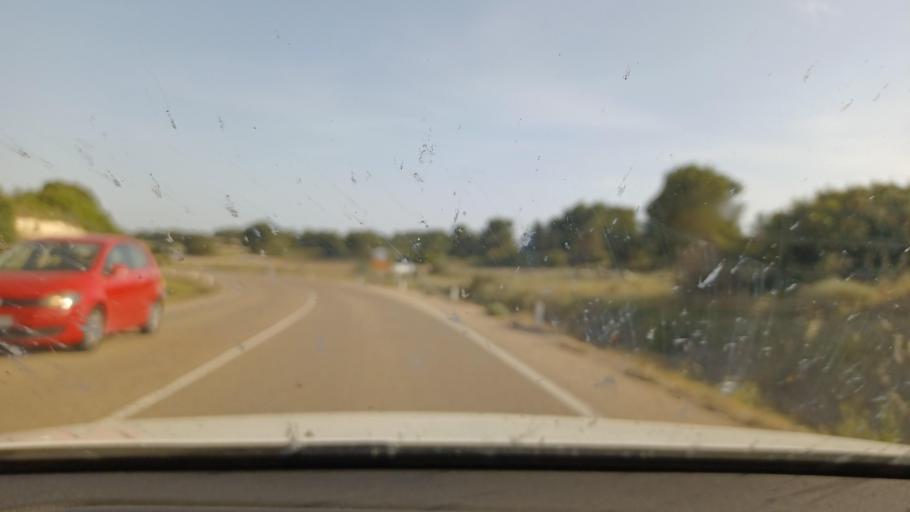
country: ES
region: Aragon
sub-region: Provincia de Zaragoza
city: Chiprana
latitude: 41.3644
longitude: -0.1075
